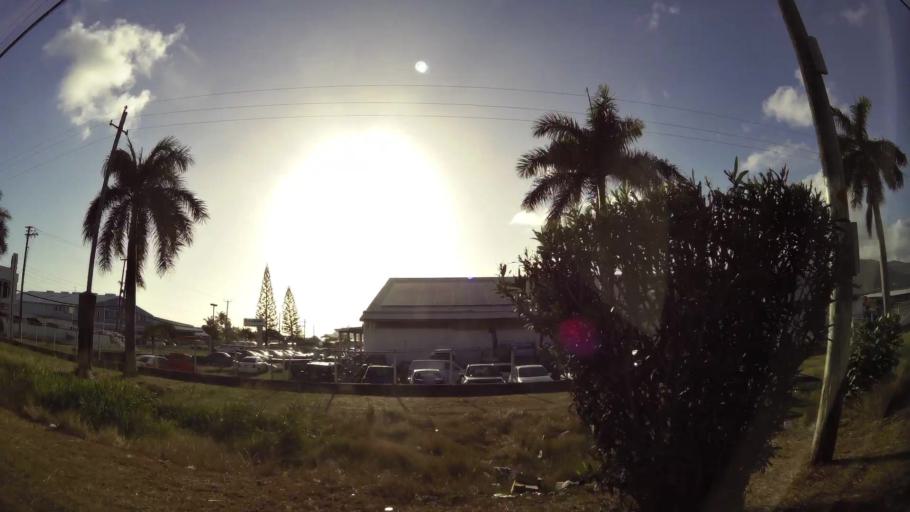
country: KN
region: Saint George Basseterre
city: Basseterre
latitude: 17.2956
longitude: -62.7085
